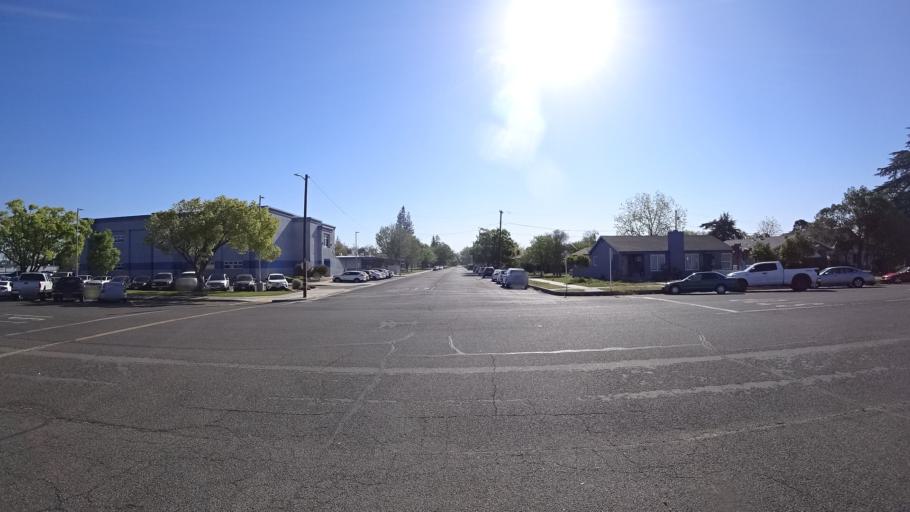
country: US
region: California
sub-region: Glenn County
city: Orland
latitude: 39.7510
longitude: -122.1929
